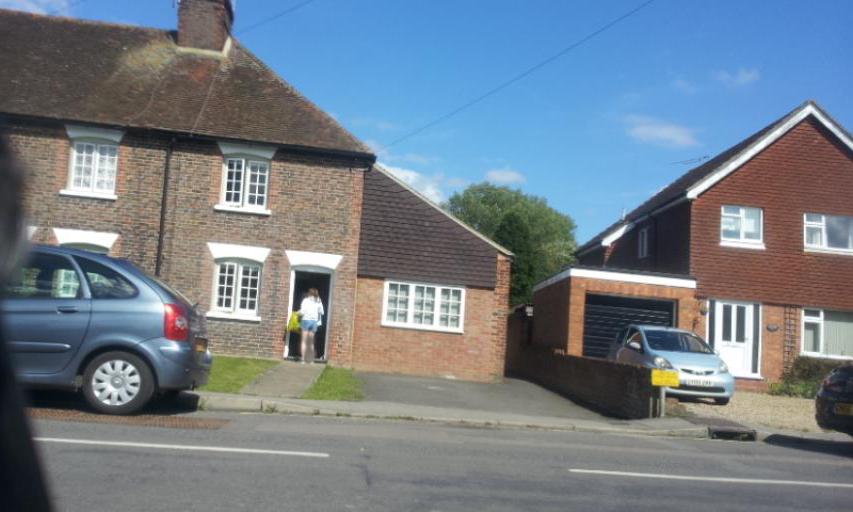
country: GB
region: England
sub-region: Kent
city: Marden
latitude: 51.1752
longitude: 0.4903
